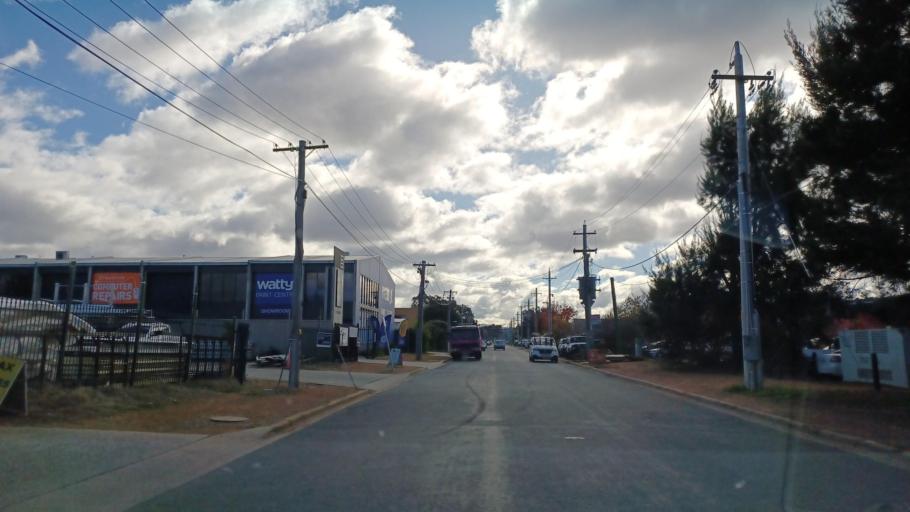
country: AU
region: Australian Capital Territory
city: Kaleen
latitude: -35.2204
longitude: 149.1435
